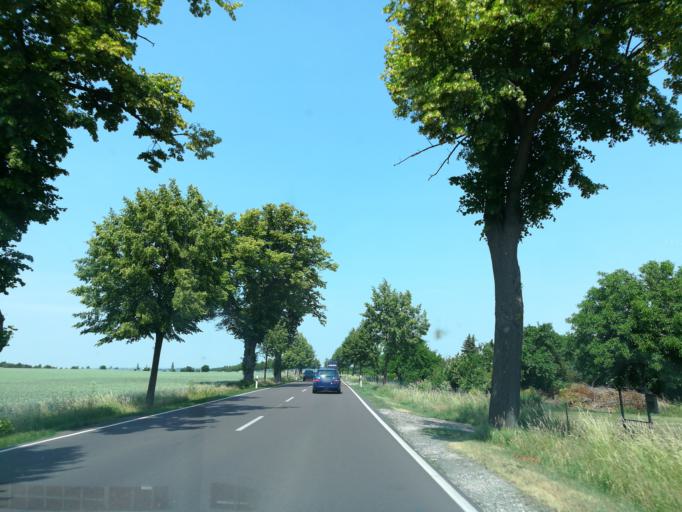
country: DE
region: Saxony-Anhalt
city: Schneidlingen
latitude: 51.8990
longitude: 11.4398
